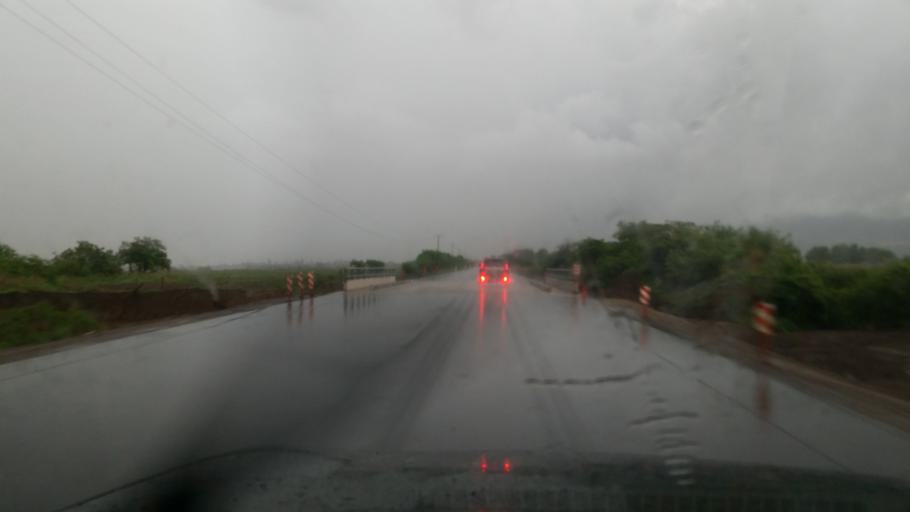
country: NI
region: Chinandega
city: Chichigalpa
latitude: 12.7783
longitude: -86.9256
